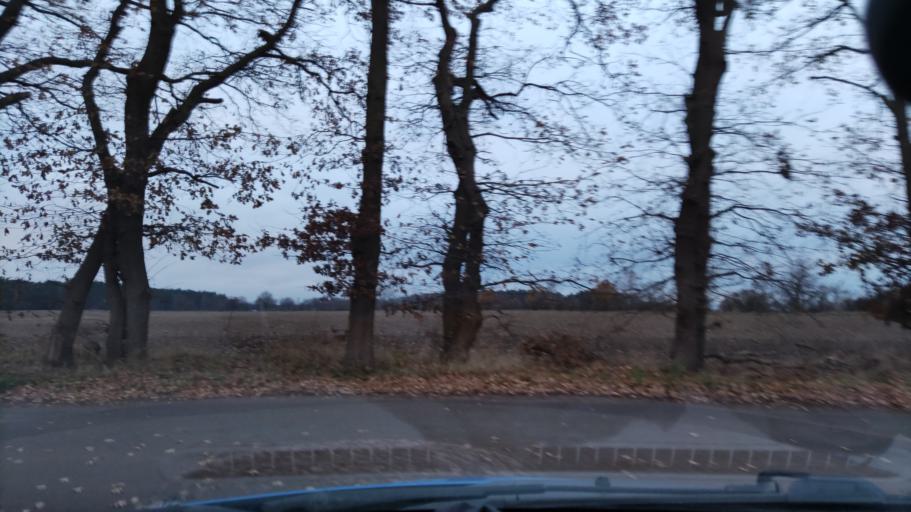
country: DE
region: Lower Saxony
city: Vogelsen
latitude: 53.2693
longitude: 10.3531
